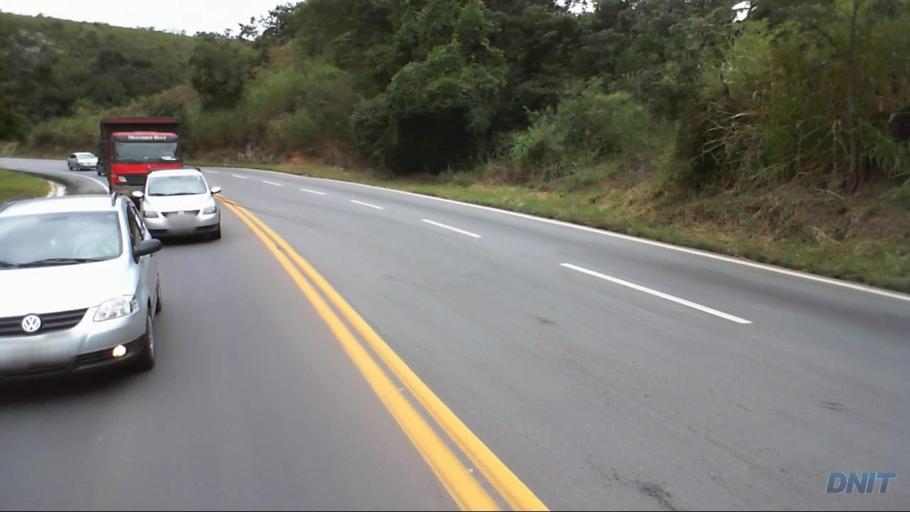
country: BR
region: Minas Gerais
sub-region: Joao Monlevade
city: Joao Monlevade
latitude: -19.8594
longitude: -43.2255
